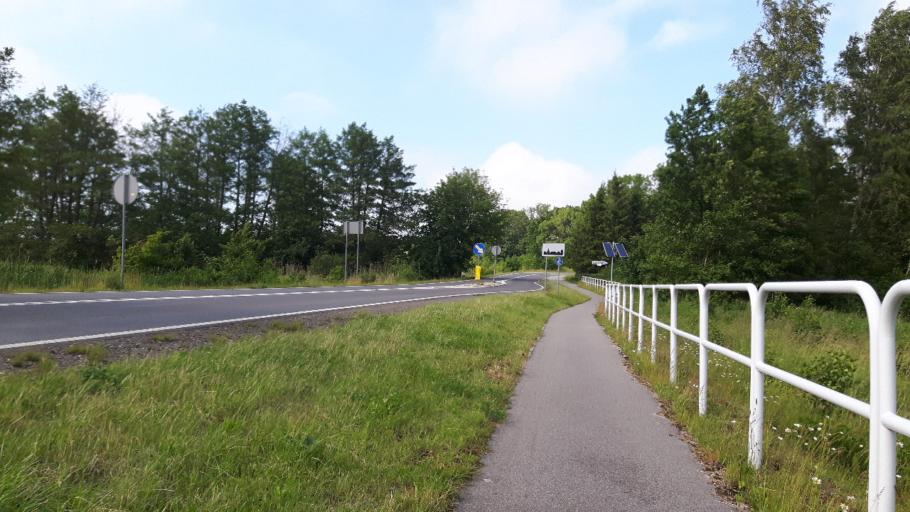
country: PL
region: West Pomeranian Voivodeship
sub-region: Powiat slawienski
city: Darlowo
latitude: 54.3513
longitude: 16.3333
